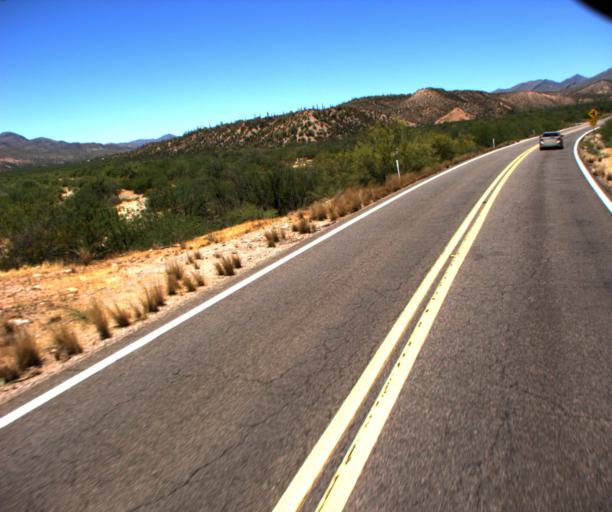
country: US
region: Arizona
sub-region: Pinal County
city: Kearny
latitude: 33.1133
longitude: -110.7696
